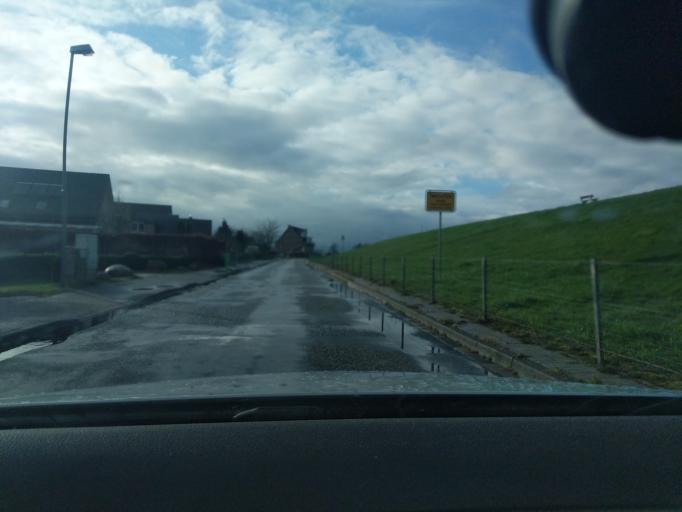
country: DE
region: Schleswig-Holstein
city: Haseldorf
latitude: 53.5923
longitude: 9.5733
